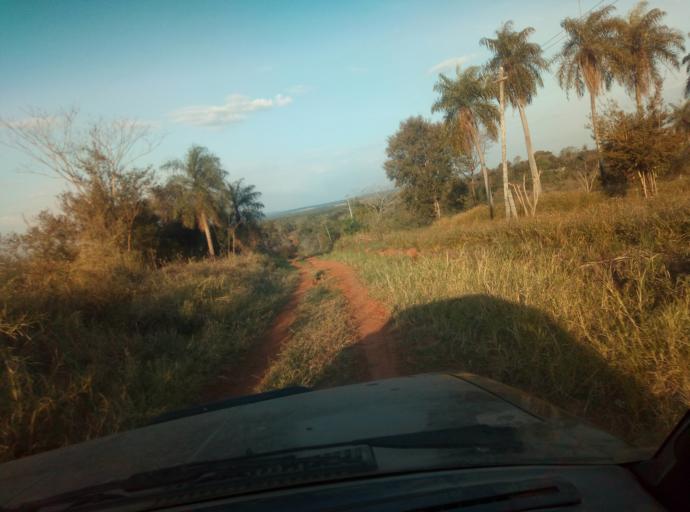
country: PY
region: Caaguazu
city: Doctor Cecilio Baez
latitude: -25.1529
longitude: -56.2409
